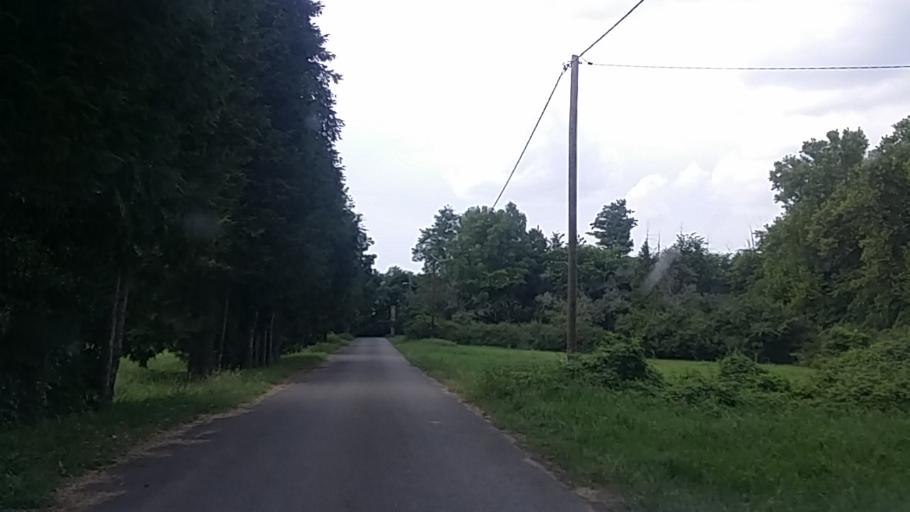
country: HU
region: Tolna
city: Szedres
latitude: 46.5213
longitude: 18.6346
